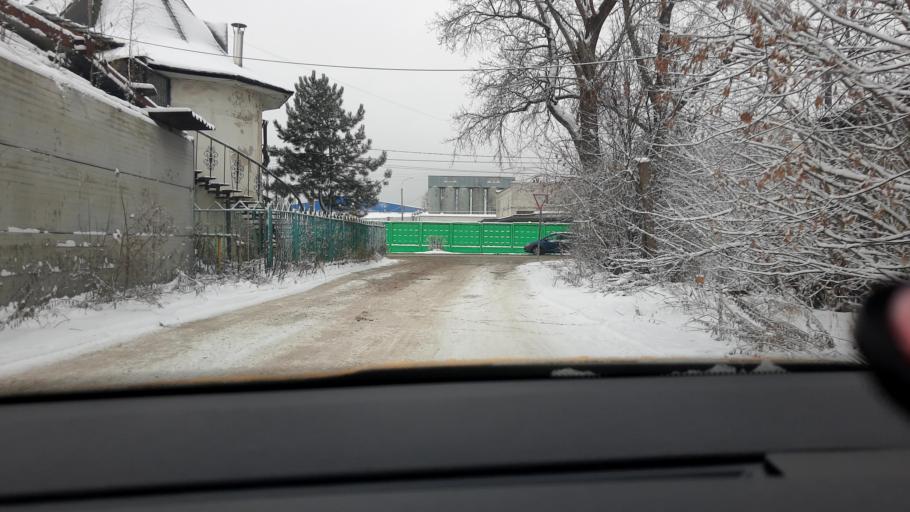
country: RU
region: Moskovskaya
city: Ivanteyevka
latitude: 55.9707
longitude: 37.9278
